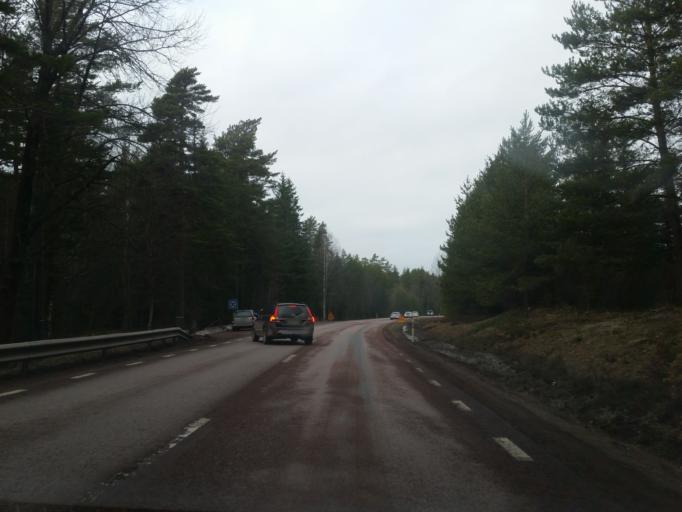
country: SE
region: Dalarna
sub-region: Mora Kommun
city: Mora
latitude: 61.0515
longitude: 14.4364
